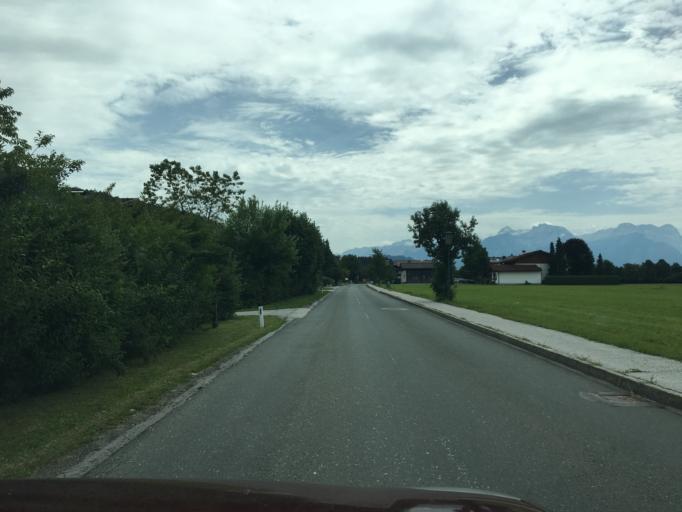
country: AT
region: Salzburg
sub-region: Politischer Bezirk Hallein
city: Adnet
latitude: 47.6653
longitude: 13.1365
